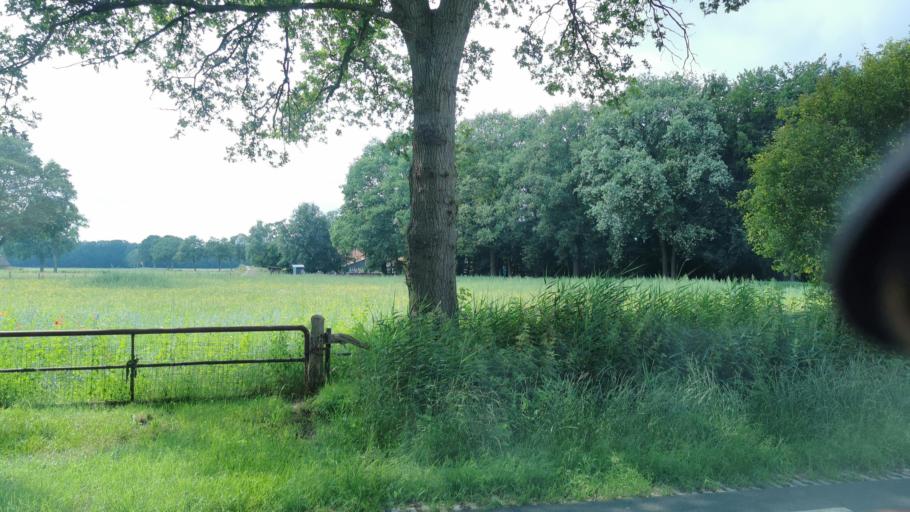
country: NL
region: Overijssel
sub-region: Gemeente Losser
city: Losser
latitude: 52.2524
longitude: 6.9837
